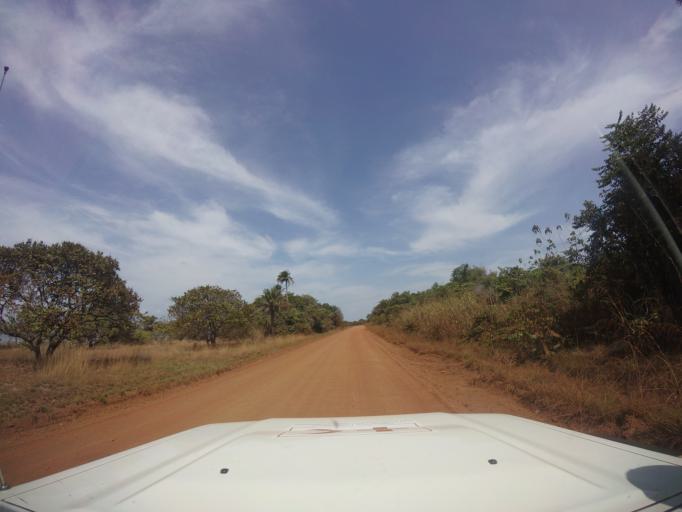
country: LR
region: Grand Cape Mount
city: Robertsport
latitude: 6.6879
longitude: -11.2530
